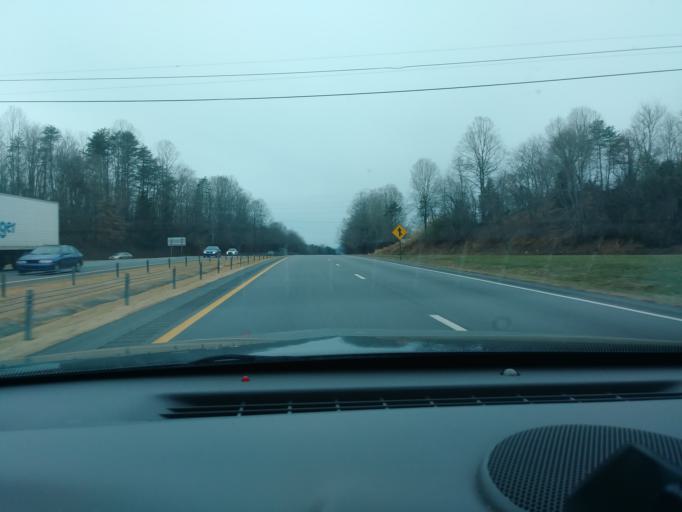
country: US
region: North Carolina
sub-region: Wilkes County
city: Wilkesboro
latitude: 36.1371
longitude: -81.1629
